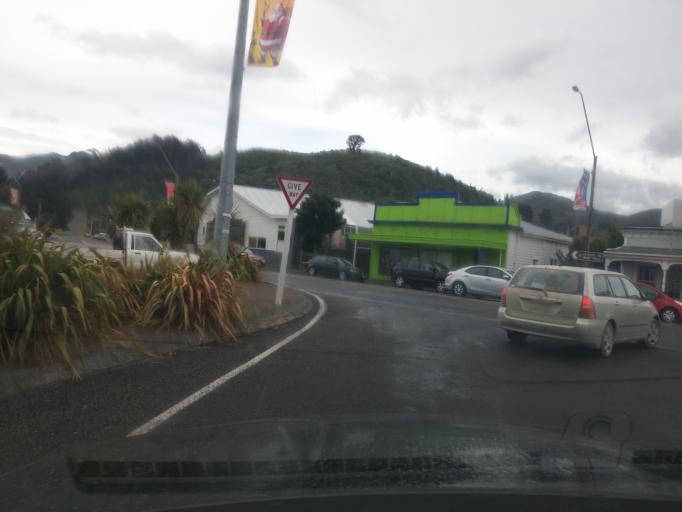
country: NZ
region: Wellington
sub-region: Upper Hutt City
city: Upper Hutt
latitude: -41.1169
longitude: 175.3225
